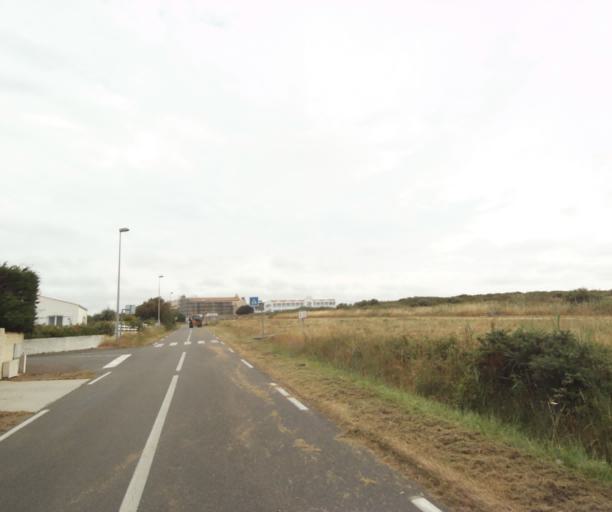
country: FR
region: Pays de la Loire
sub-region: Departement de la Vendee
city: Chateau-d'Olonne
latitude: 46.4664
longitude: -1.7316
